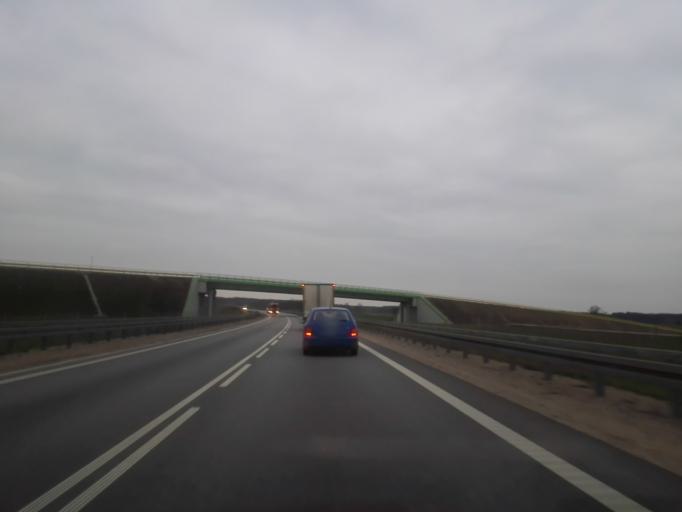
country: PL
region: Podlasie
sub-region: Powiat kolnenski
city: Stawiski
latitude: 53.3741
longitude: 22.1453
